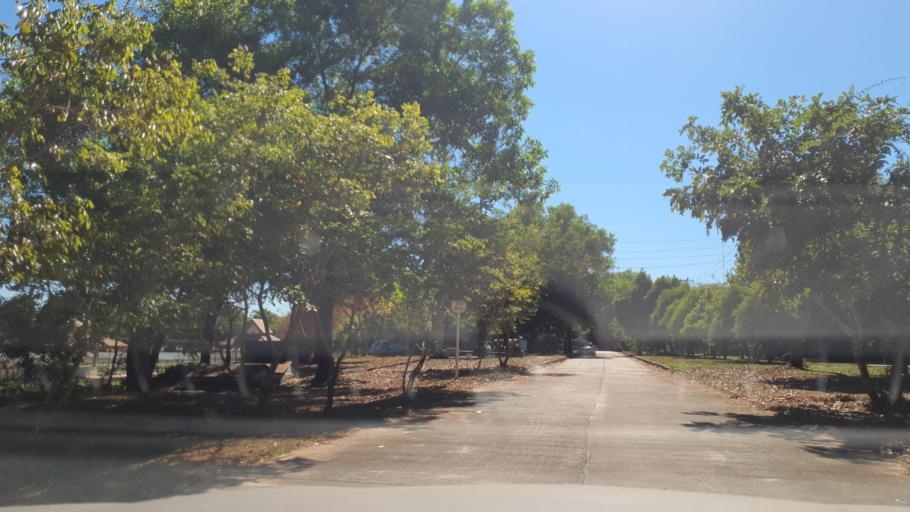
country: TH
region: Nakhon Phanom
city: Nakhon Phanom
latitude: 17.3748
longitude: 104.7376
